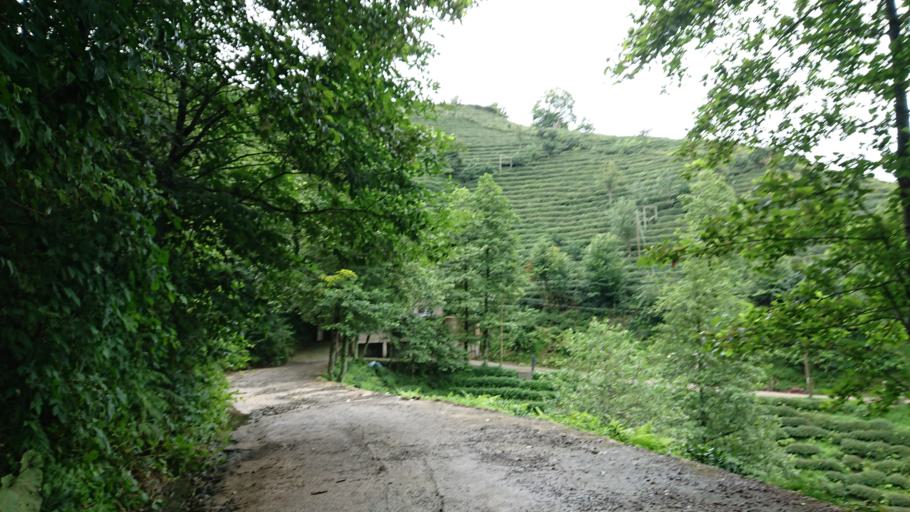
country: TR
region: Rize
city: Rize
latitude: 40.9768
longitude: 40.4854
